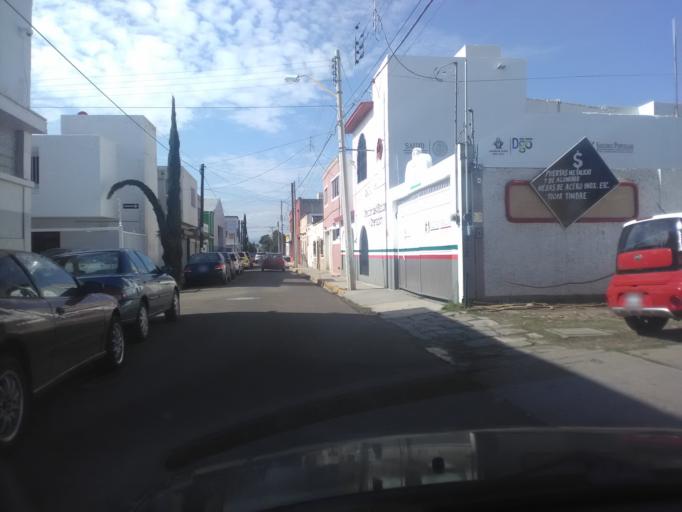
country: MX
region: Durango
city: Victoria de Durango
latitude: 24.0260
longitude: -104.6587
